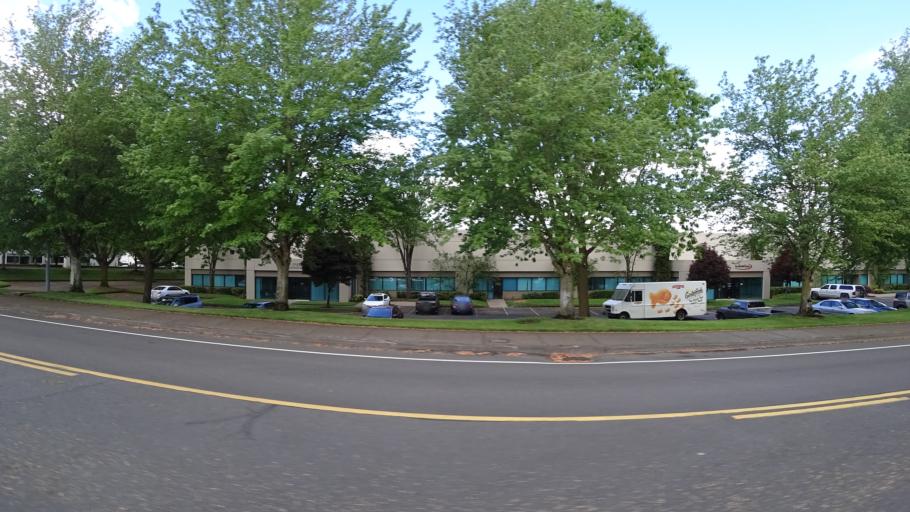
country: US
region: Oregon
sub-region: Washington County
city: Durham
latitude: 45.3995
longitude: -122.7491
